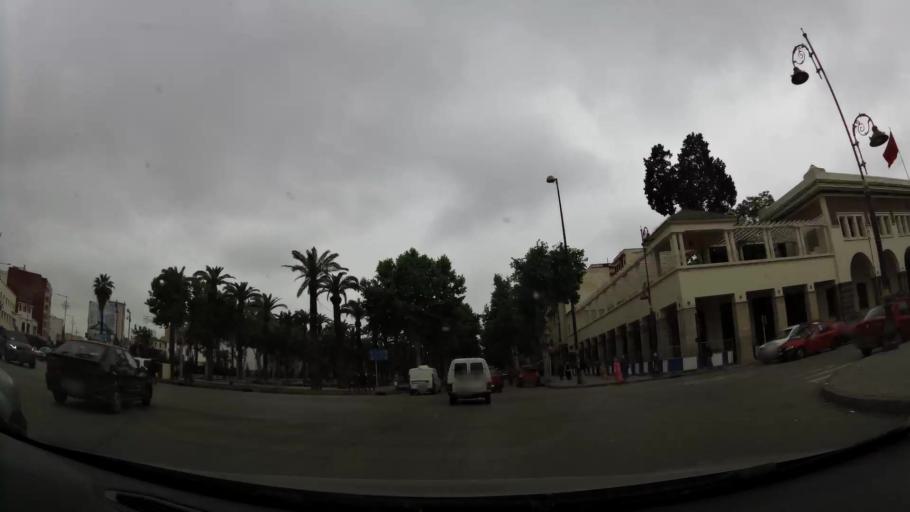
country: MA
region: Fes-Boulemane
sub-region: Fes
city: Fes
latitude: 34.0415
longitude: -4.9997
